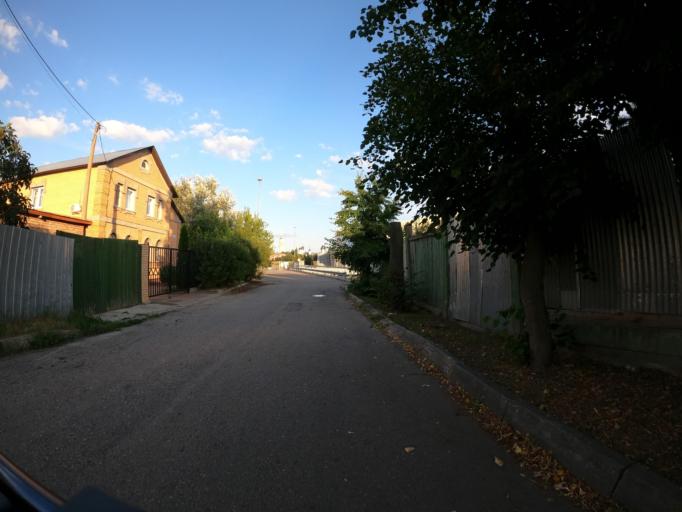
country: RU
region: Moskovskaya
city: Raduzhnyy
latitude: 55.1081
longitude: 38.7510
